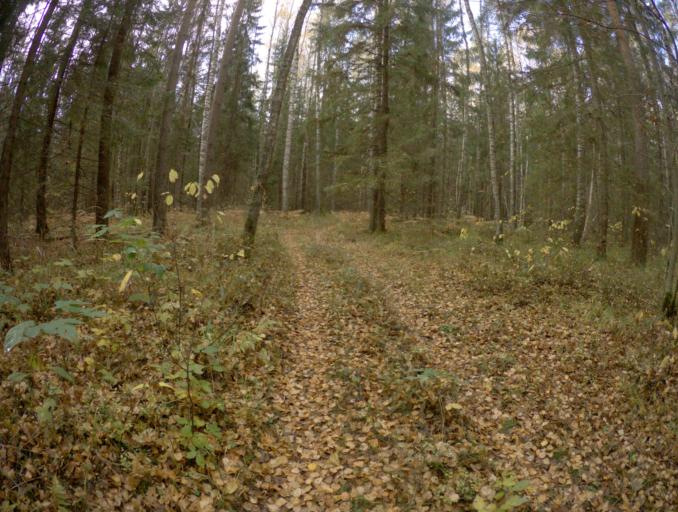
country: RU
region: Vladimir
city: Raduzhnyy
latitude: 55.9645
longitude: 40.3571
